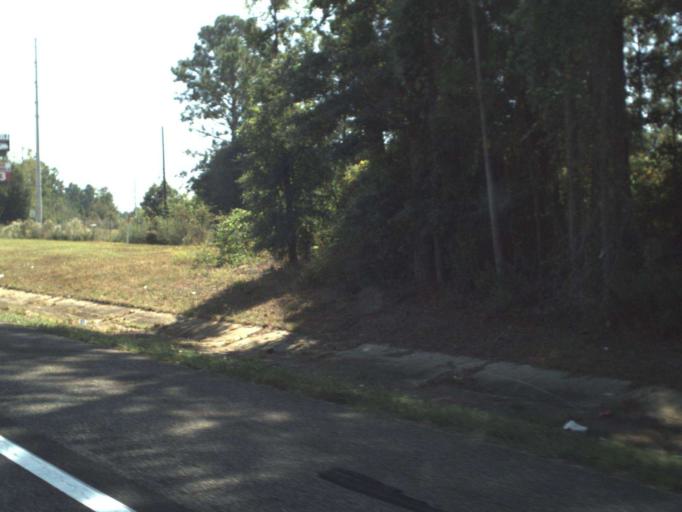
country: US
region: Florida
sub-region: Escambia County
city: Ensley
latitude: 30.5145
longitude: -87.3008
